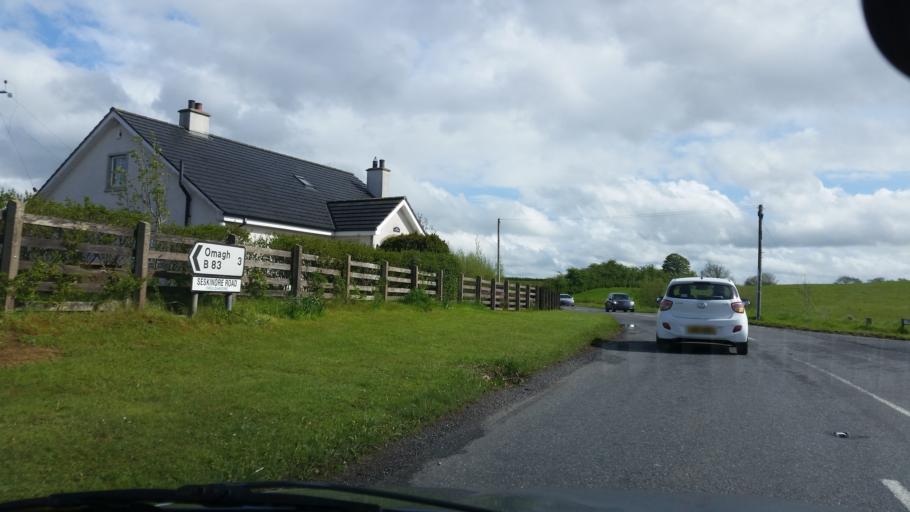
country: GB
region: Northern Ireland
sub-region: Omagh District
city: Omagh
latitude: 54.5622
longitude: -7.2755
